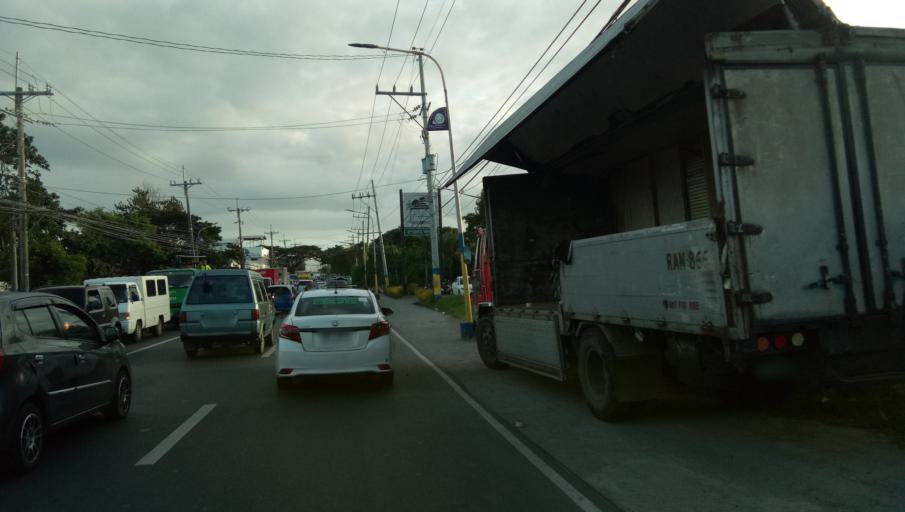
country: PH
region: Calabarzon
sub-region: Province of Cavite
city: Dasmarinas
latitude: 14.3789
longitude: 120.9789
